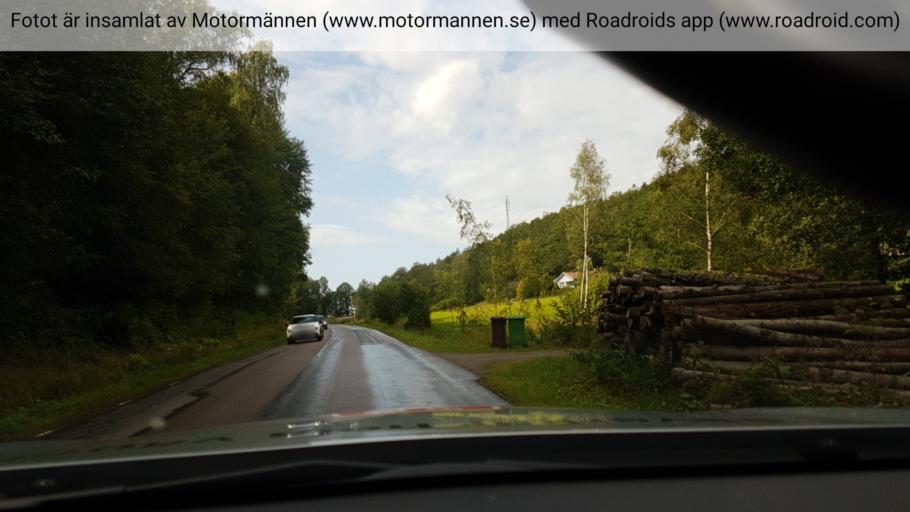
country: SE
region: Vaestra Goetaland
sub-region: Uddevalla Kommun
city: Ljungskile
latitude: 58.2250
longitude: 11.8856
